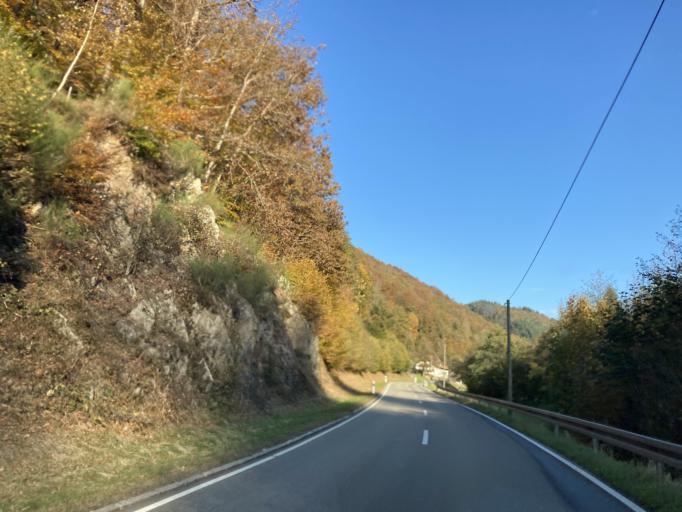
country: DE
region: Baden-Wuerttemberg
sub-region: Freiburg Region
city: Buchenbach
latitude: 47.9719
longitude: 8.0368
